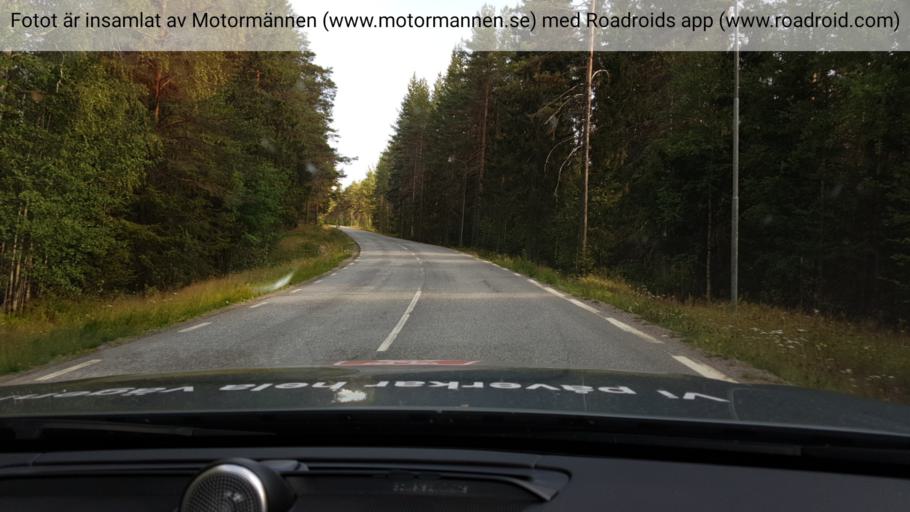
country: SE
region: Vaesterbotten
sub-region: Dorotea Kommun
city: Dorotea
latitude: 63.9159
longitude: 16.3450
